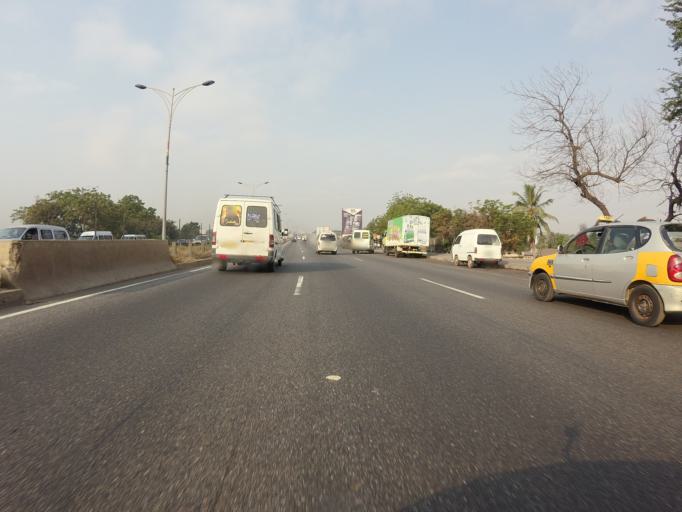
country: GH
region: Greater Accra
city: Dome
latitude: 5.6133
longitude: -0.2252
